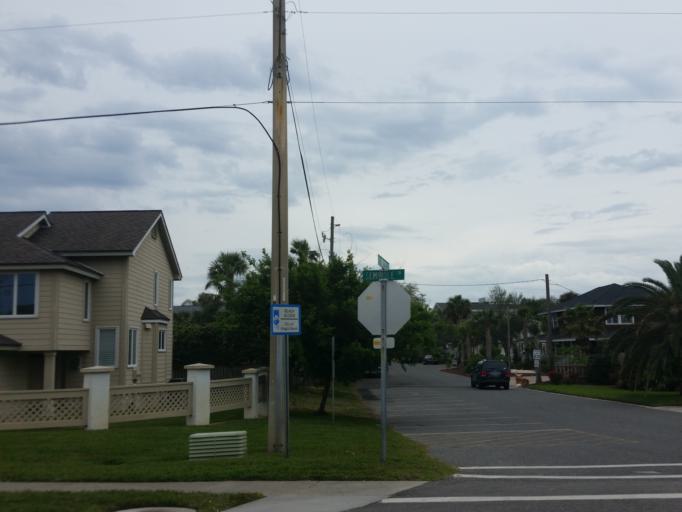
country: US
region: Florida
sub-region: Duval County
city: Atlantic Beach
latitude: 30.3468
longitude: -81.3995
